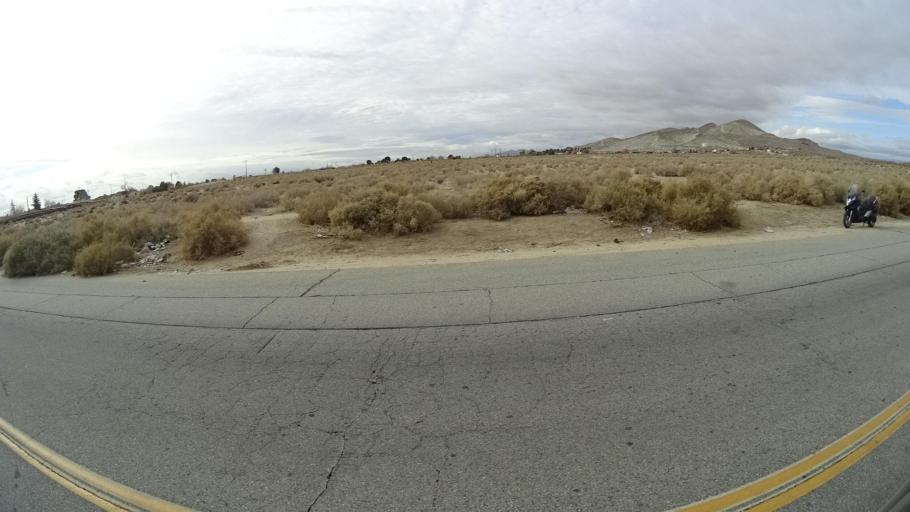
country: US
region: California
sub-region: Kern County
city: Rosamond
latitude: 34.8696
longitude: -118.1579
